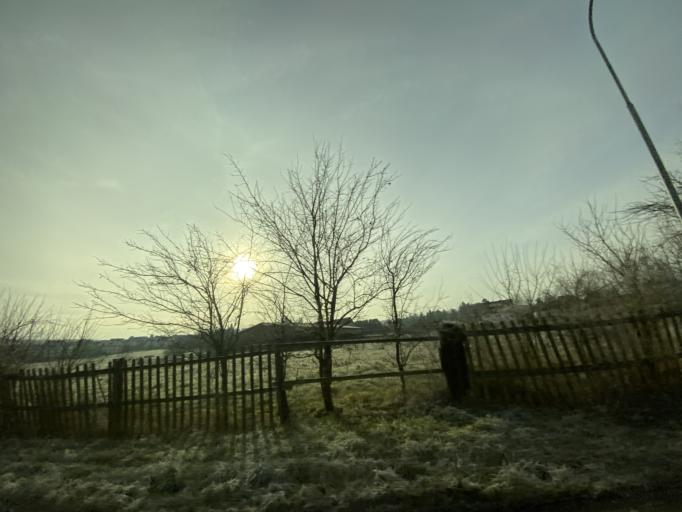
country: DE
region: Hesse
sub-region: Regierungsbezirk Giessen
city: Ebsdorfergrund
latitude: 50.7620
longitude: 8.8846
